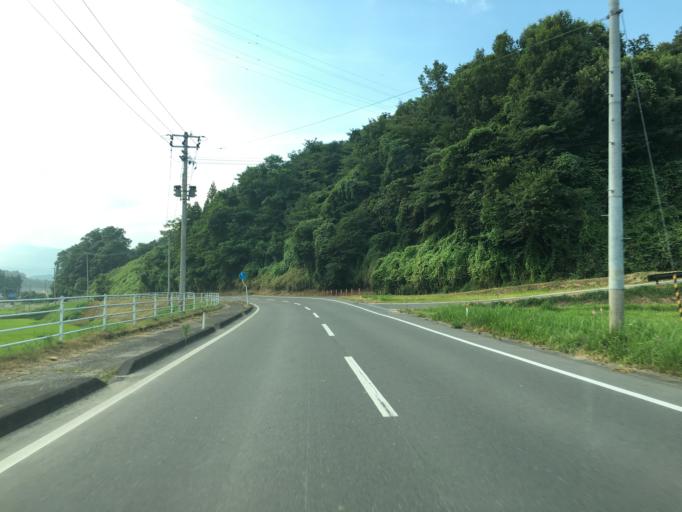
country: JP
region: Fukushima
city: Nihommatsu
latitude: 37.5493
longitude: 140.4411
